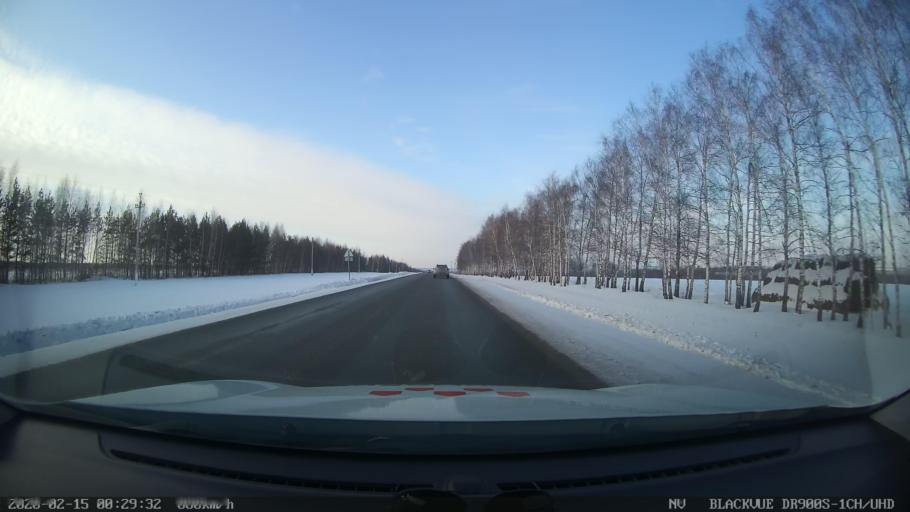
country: RU
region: Tatarstan
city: Verkhniy Uslon
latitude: 55.6515
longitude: 48.8674
